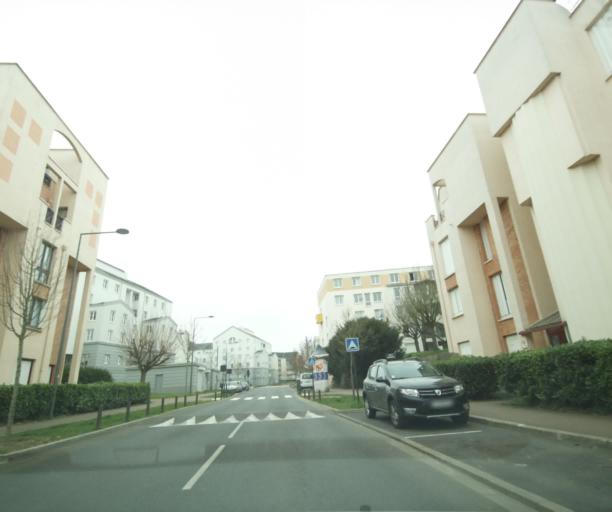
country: FR
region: Ile-de-France
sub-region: Departement du Val-d'Oise
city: Vaureal
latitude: 49.0491
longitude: 2.0283
